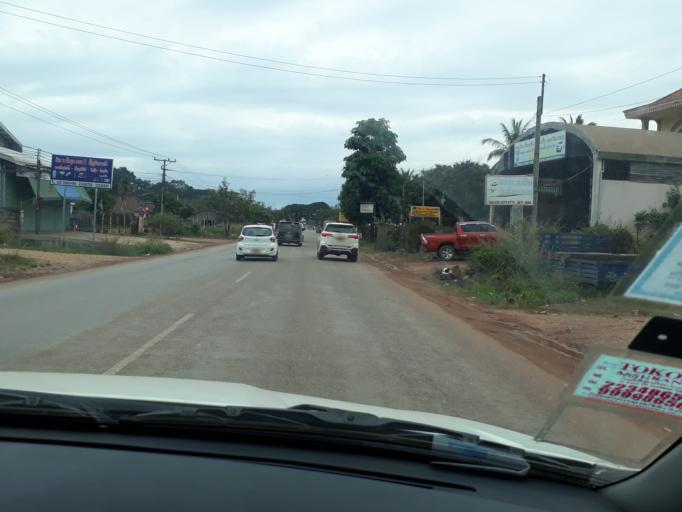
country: LA
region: Vientiane
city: Muang Phon-Hong
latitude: 18.3392
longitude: 102.4342
